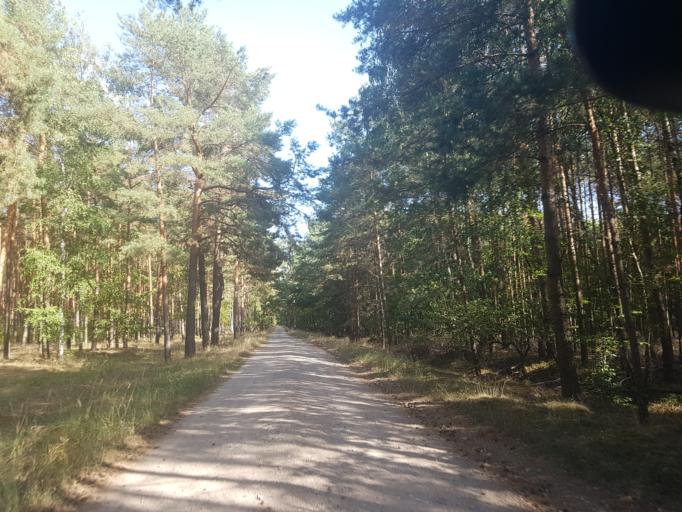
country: DE
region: Saxony-Anhalt
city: Seyda
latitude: 51.8792
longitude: 12.9471
